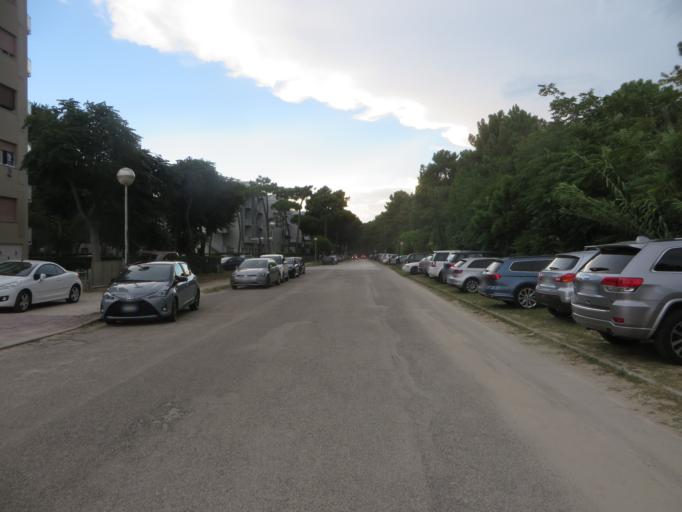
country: IT
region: Emilia-Romagna
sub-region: Provincia di Ravenna
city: Cervia
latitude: 44.2932
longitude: 12.3474
